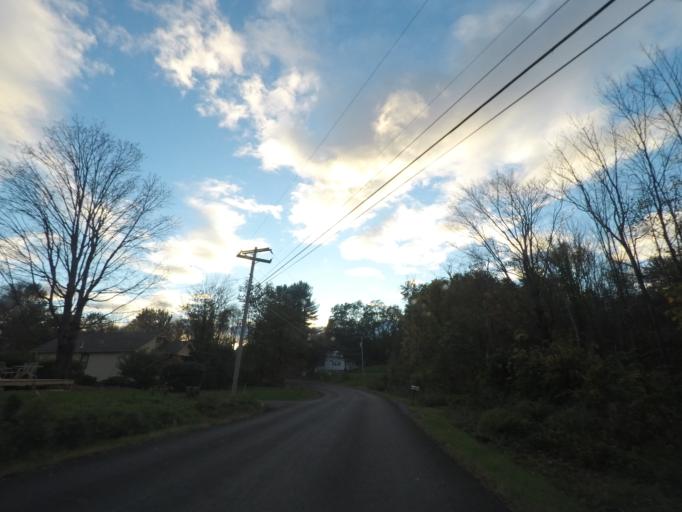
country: US
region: New York
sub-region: Rensselaer County
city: Nassau
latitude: 42.5282
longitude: -73.5855
